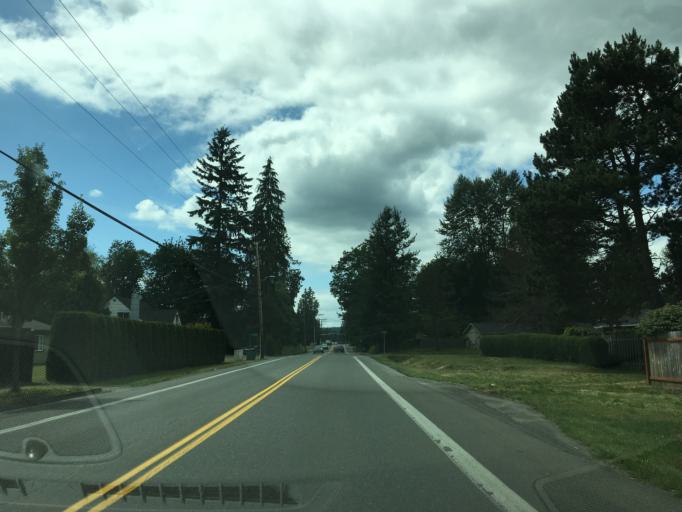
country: US
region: Washington
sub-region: Snohomish County
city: Marysville
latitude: 48.0748
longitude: -122.1518
